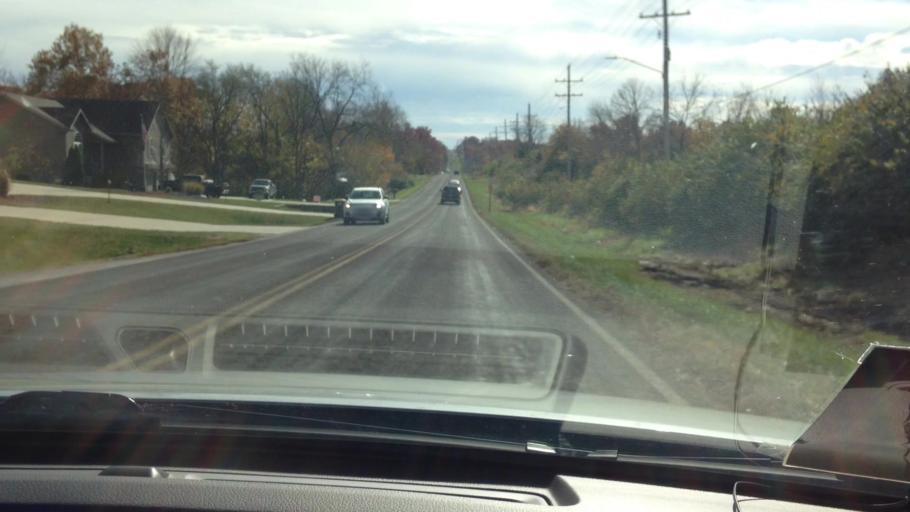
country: US
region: Kansas
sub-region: Leavenworth County
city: Lansing
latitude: 39.2579
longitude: -94.9188
